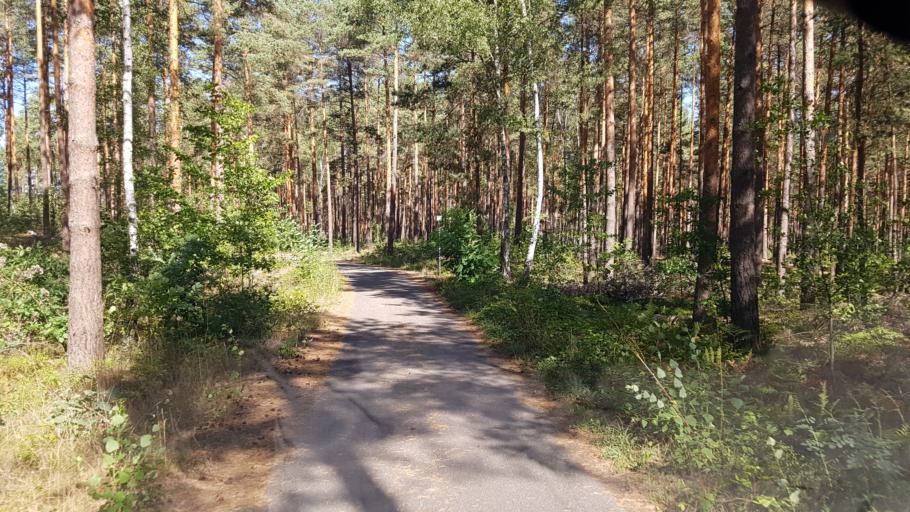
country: DE
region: Brandenburg
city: Calau
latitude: 51.7077
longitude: 13.9974
